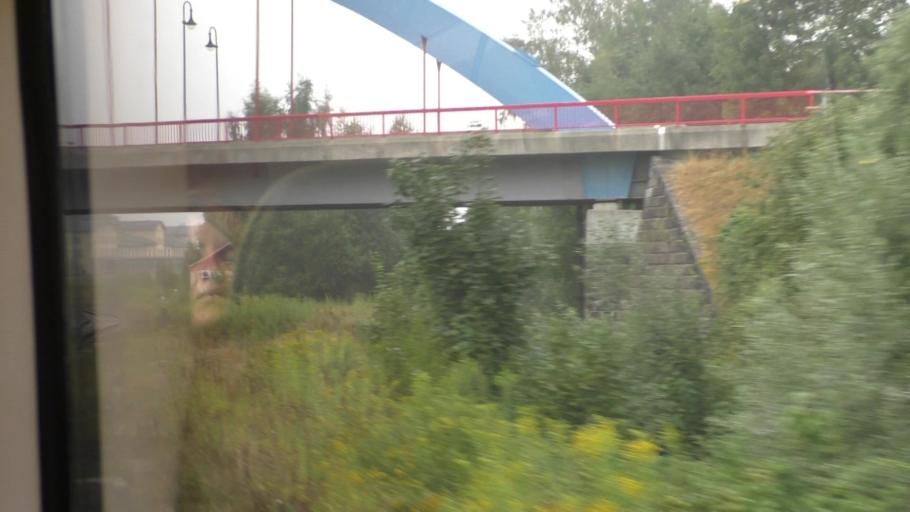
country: DE
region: Saxony
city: Ebersbach
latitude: 50.9996
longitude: 14.5794
